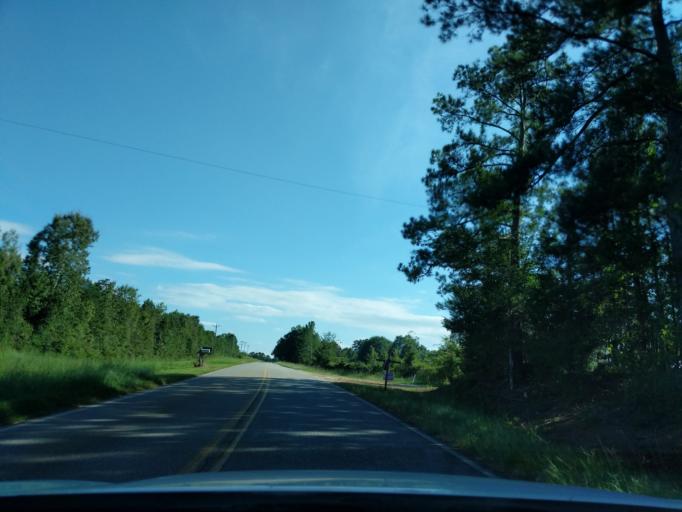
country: US
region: Georgia
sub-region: Oglethorpe County
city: Lexington
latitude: 33.8841
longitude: -82.9928
